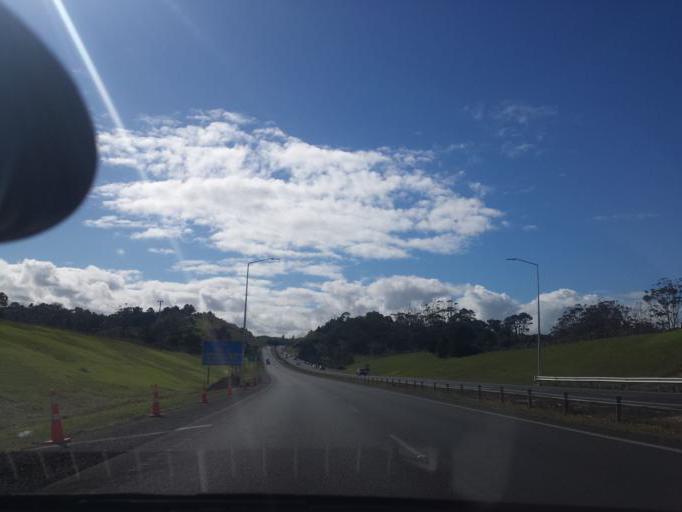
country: NZ
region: Auckland
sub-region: Auckland
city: Rothesay Bay
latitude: -36.6022
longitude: 174.6623
